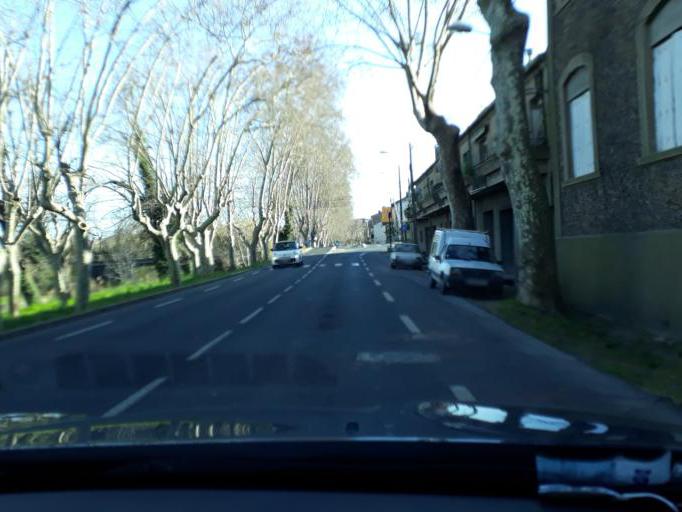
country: FR
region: Languedoc-Roussillon
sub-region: Departement de l'Herault
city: Agde
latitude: 43.3187
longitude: 3.4677
